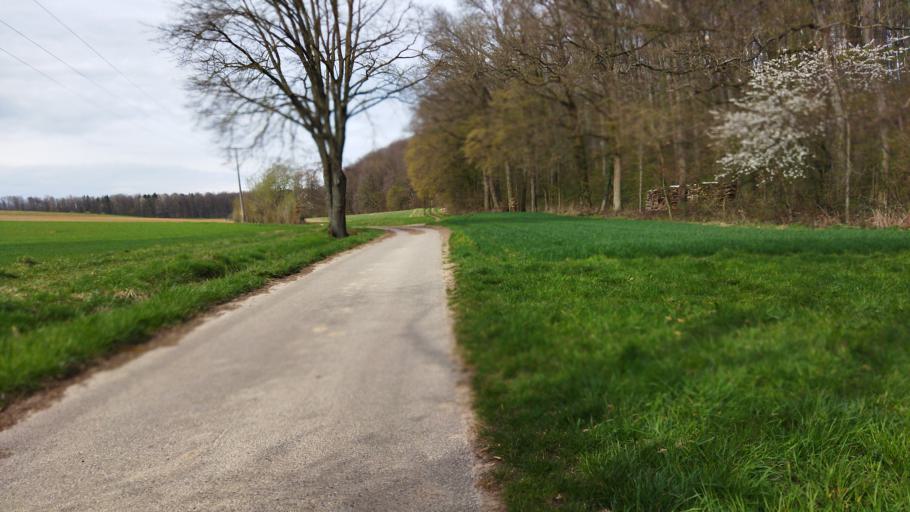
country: DE
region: Baden-Wuerttemberg
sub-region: Regierungsbezirk Stuttgart
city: Gundelsheim
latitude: 49.2855
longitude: 9.1858
